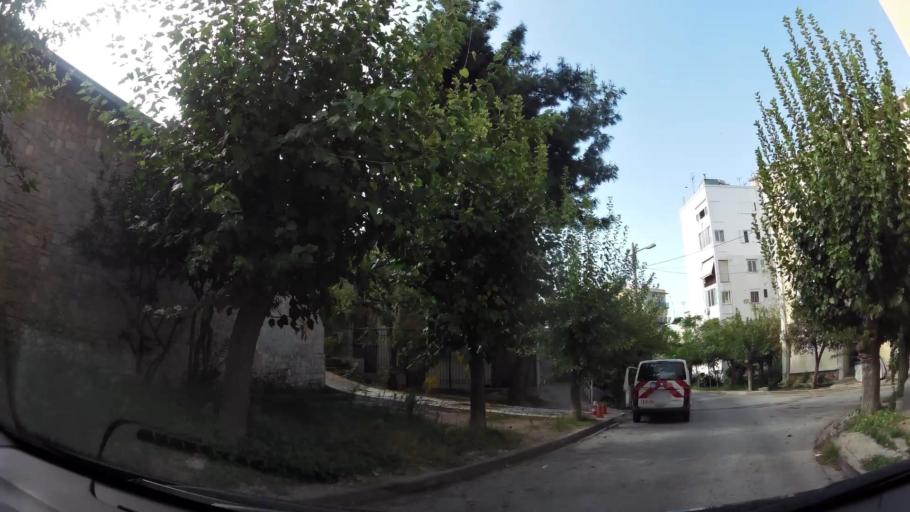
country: GR
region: Attica
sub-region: Nomarchia Athinas
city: Ilioupoli
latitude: 37.9476
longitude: 23.7728
